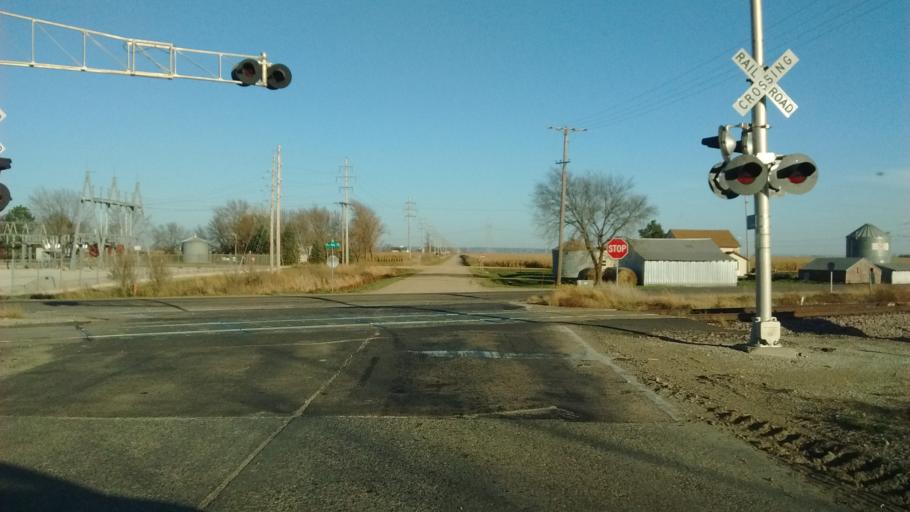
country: US
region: Iowa
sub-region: Woodbury County
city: Sergeant Bluff
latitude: 42.3302
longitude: -96.3024
